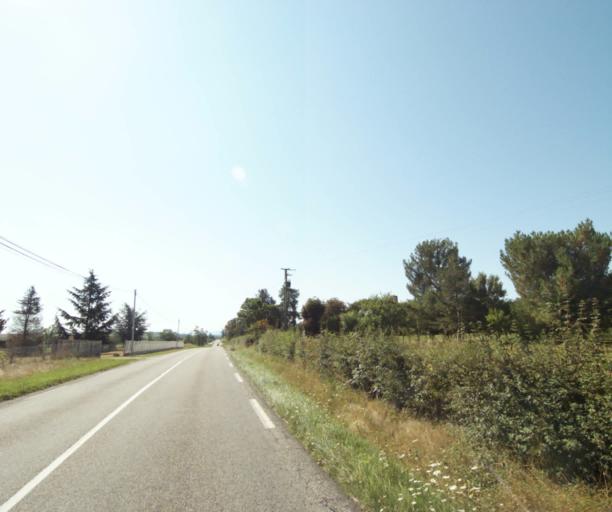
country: FR
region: Midi-Pyrenees
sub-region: Departement de l'Ariege
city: Lezat-sur-Leze
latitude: 43.2941
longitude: 1.3407
